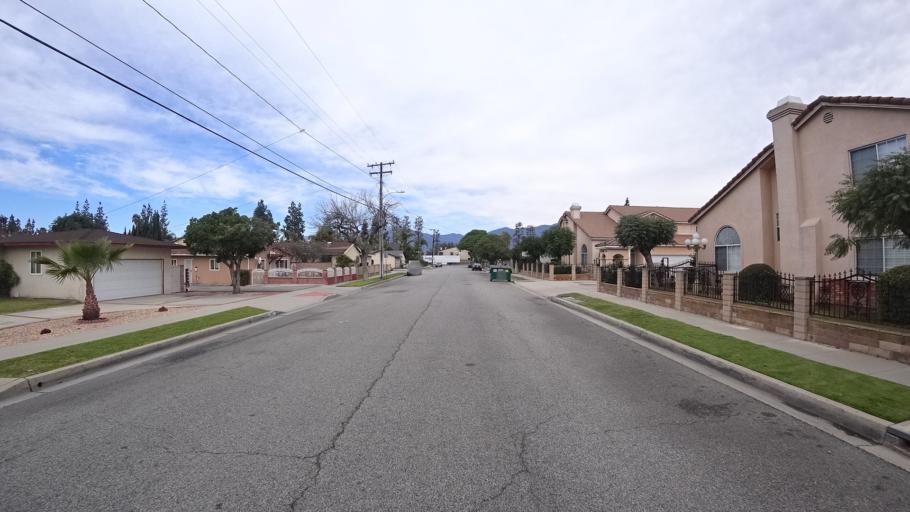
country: US
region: California
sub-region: Los Angeles County
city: Baldwin Park
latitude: 34.0808
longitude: -117.9785
